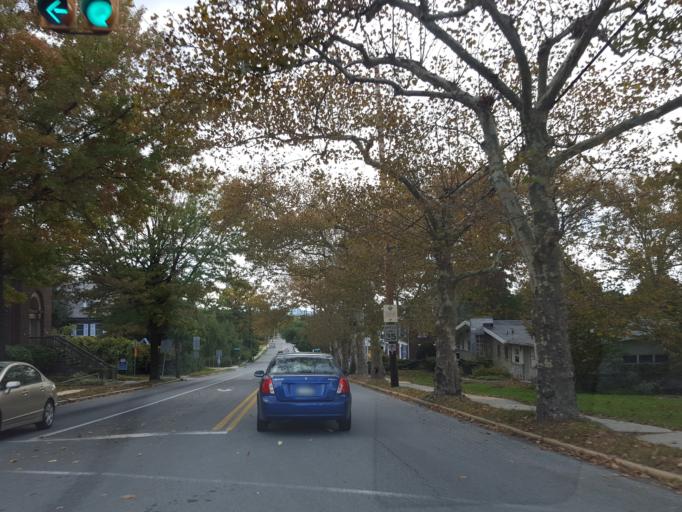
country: US
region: Pennsylvania
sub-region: York County
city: Valley View
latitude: 39.9483
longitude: -76.7119
